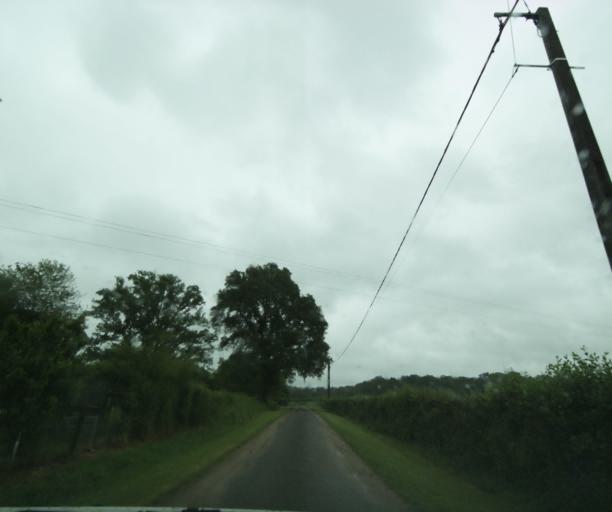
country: FR
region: Bourgogne
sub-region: Departement de Saone-et-Loire
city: Palinges
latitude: 46.5204
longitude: 4.2136
